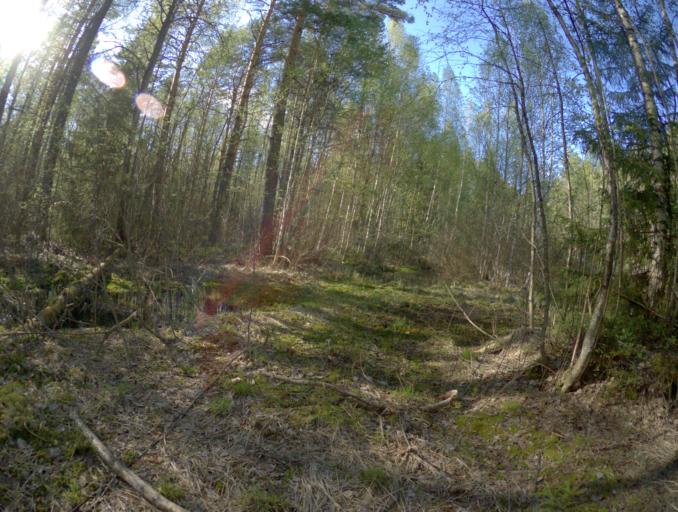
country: RU
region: Vladimir
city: Golovino
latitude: 55.9162
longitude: 40.4401
